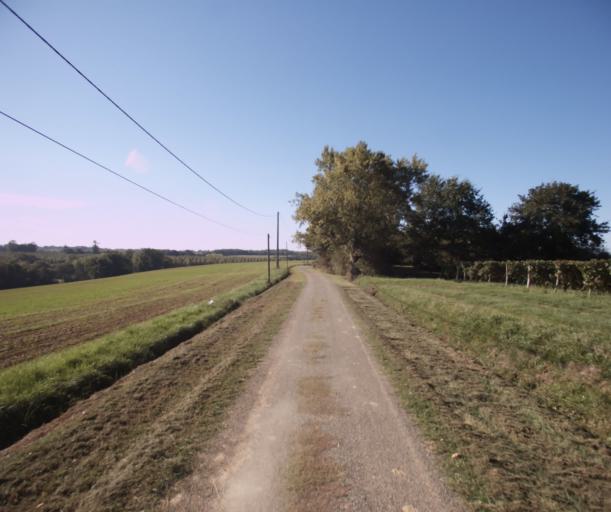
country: FR
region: Aquitaine
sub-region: Departement des Landes
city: Gabarret
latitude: 43.9046
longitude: 0.0104
